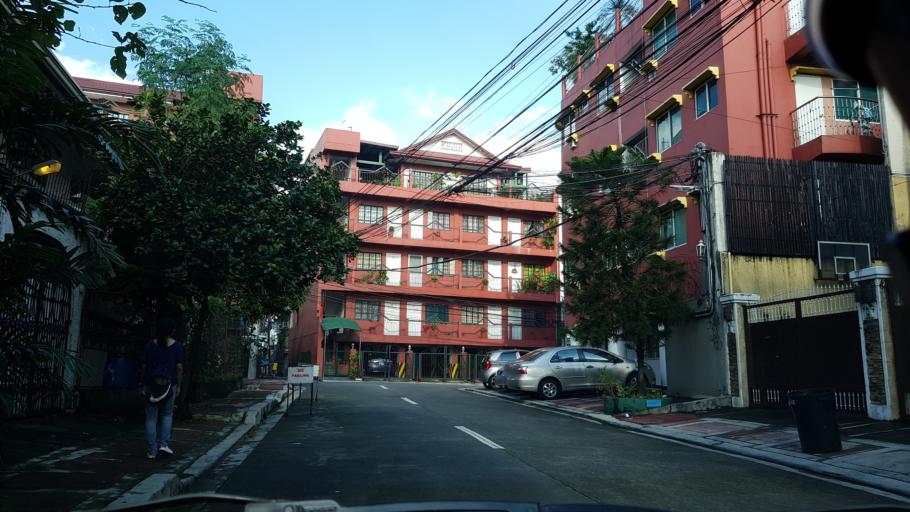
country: PH
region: Metro Manila
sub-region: Quezon City
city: Quezon City
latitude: 14.6436
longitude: 121.0521
